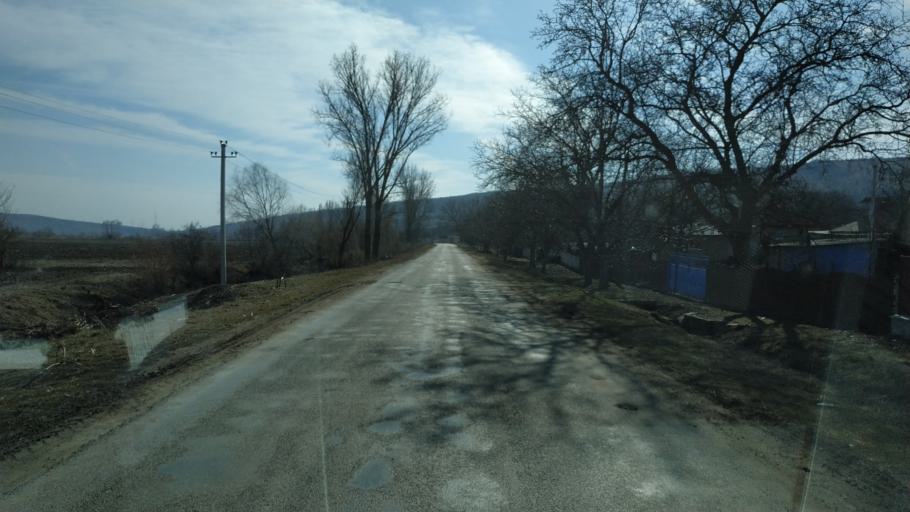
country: MD
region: Nisporeni
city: Nisporeni
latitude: 47.1518
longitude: 28.1079
